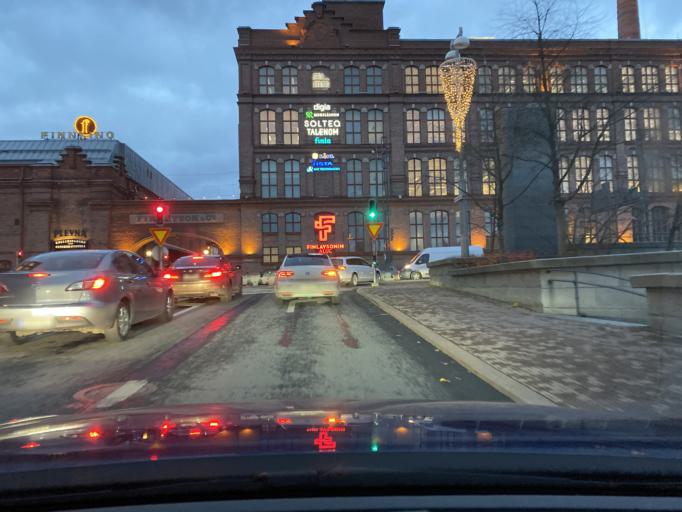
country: FI
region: Pirkanmaa
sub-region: Tampere
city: Tampere
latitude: 61.5004
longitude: 23.7592
